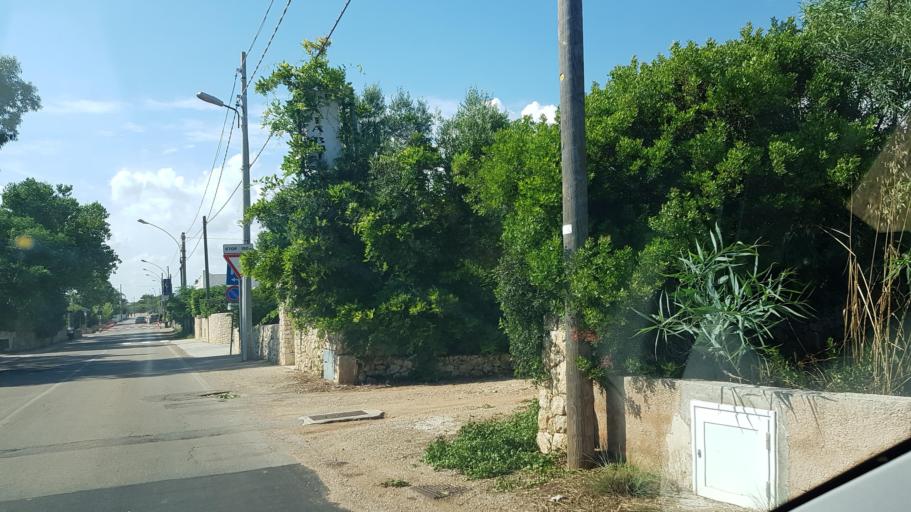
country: IT
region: Apulia
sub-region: Provincia di Lecce
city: Morciano di Leuca
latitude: 39.8131
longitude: 18.3151
